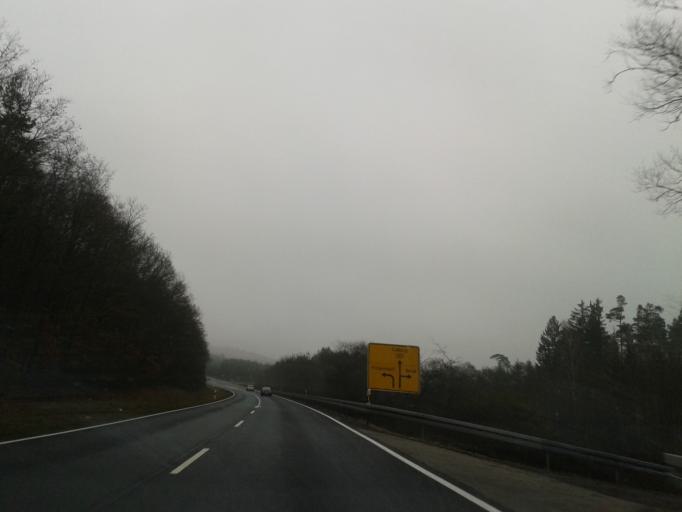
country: DE
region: Bavaria
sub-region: Regierungsbezirk Unterfranken
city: Burgpreppach
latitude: 50.1342
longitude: 10.6037
